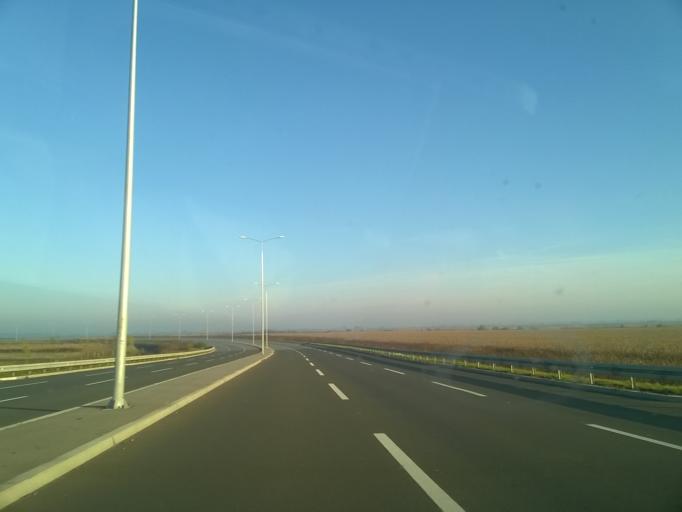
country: RS
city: Ovca
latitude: 44.9088
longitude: 20.5116
